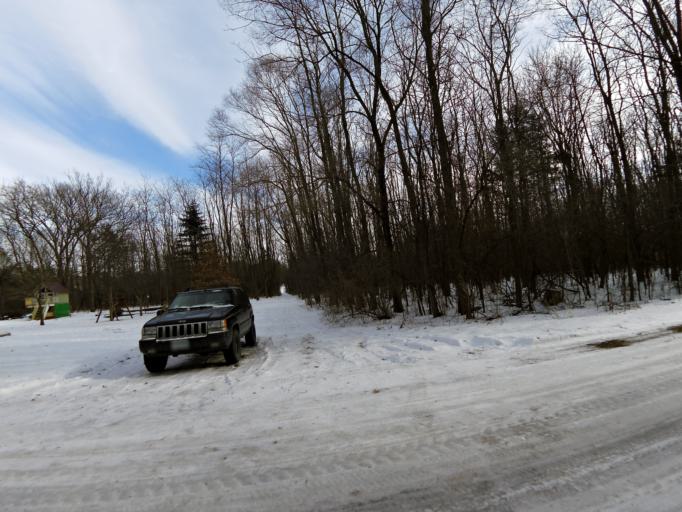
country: US
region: Minnesota
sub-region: Washington County
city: Lake Saint Croix Beach
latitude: 44.9165
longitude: -92.7698
